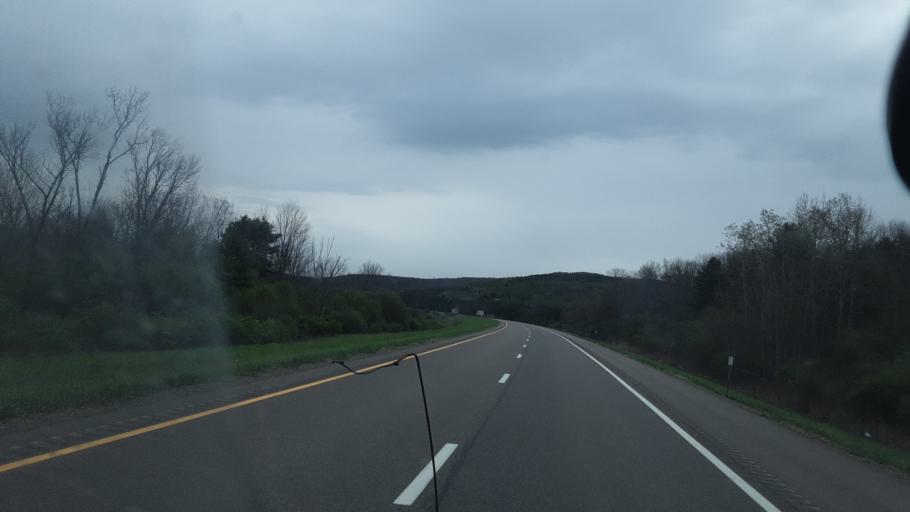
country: US
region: New York
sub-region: Allegany County
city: Belmont
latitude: 42.2932
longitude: -77.9857
